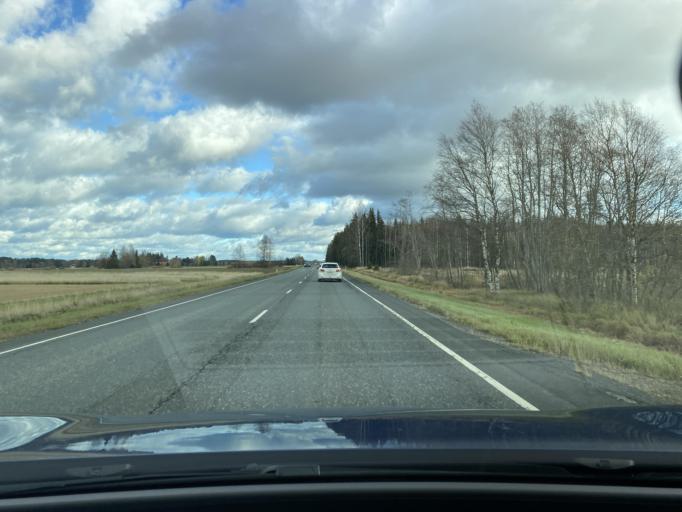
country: FI
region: Haeme
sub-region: Forssa
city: Humppila
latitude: 60.9454
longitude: 23.3053
